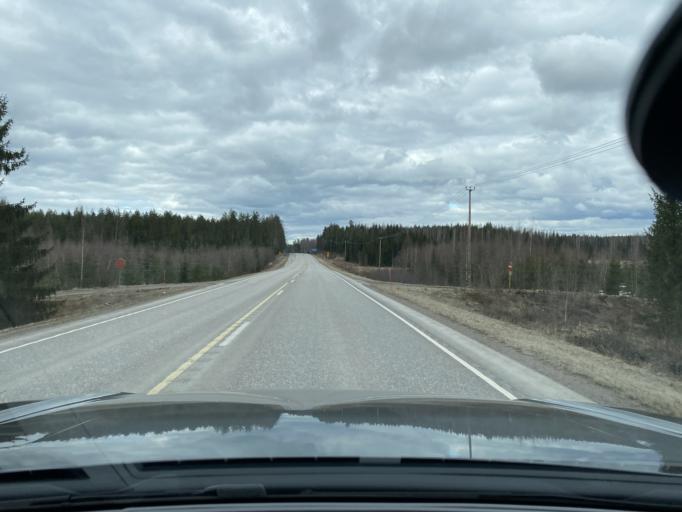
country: FI
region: Uusimaa
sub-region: Helsinki
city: Hyvinge
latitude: 60.5566
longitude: 24.8219
